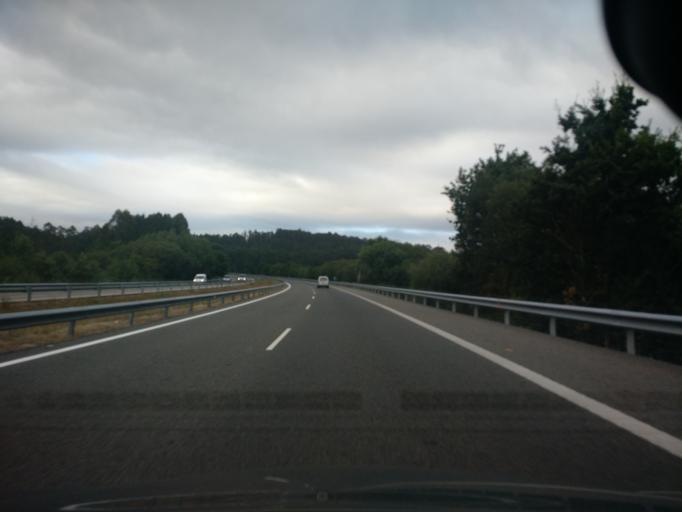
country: ES
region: Galicia
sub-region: Provincia da Coruna
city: Abegondo
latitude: 43.2263
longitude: -8.2728
